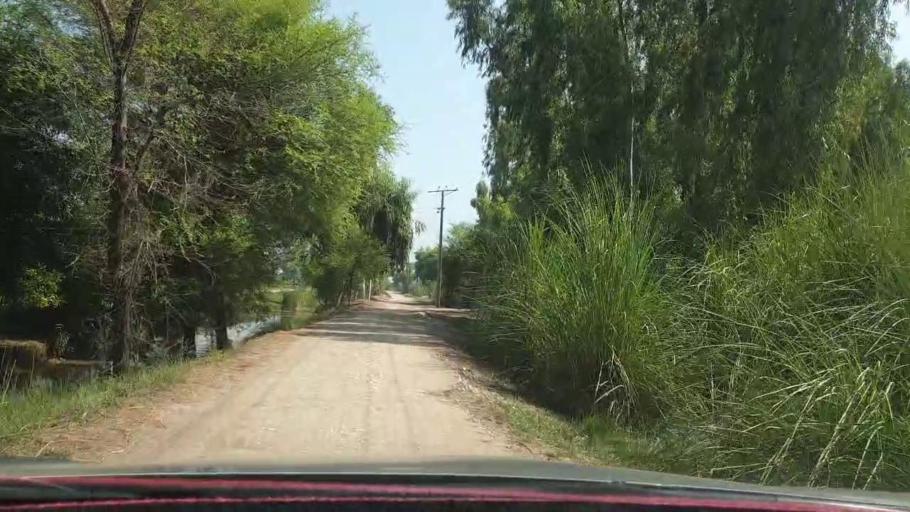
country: PK
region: Sindh
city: Warah
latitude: 27.4842
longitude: 67.8315
